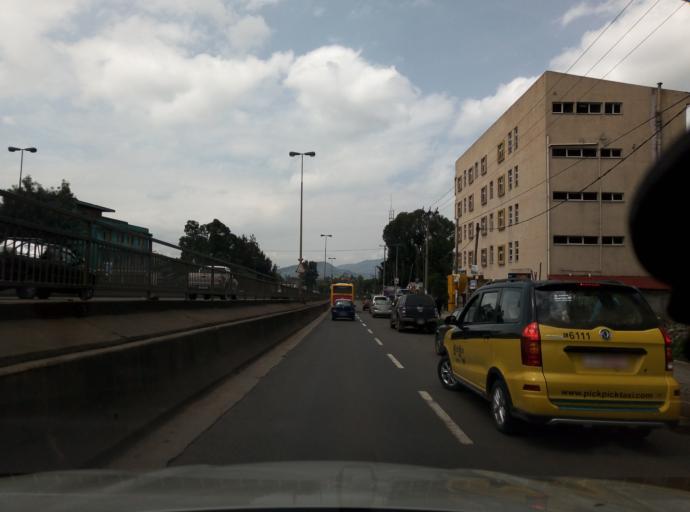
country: ET
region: Adis Abeba
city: Addis Ababa
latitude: 8.9973
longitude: 38.7185
